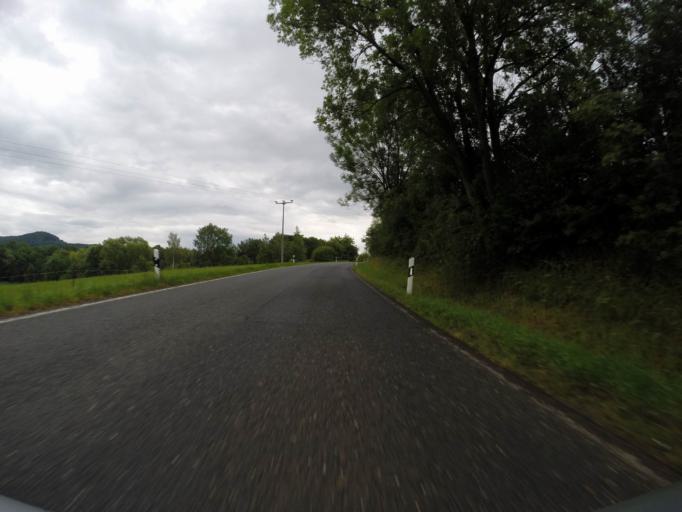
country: DE
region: Thuringia
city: Nausnitz
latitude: 50.9545
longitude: 11.7200
